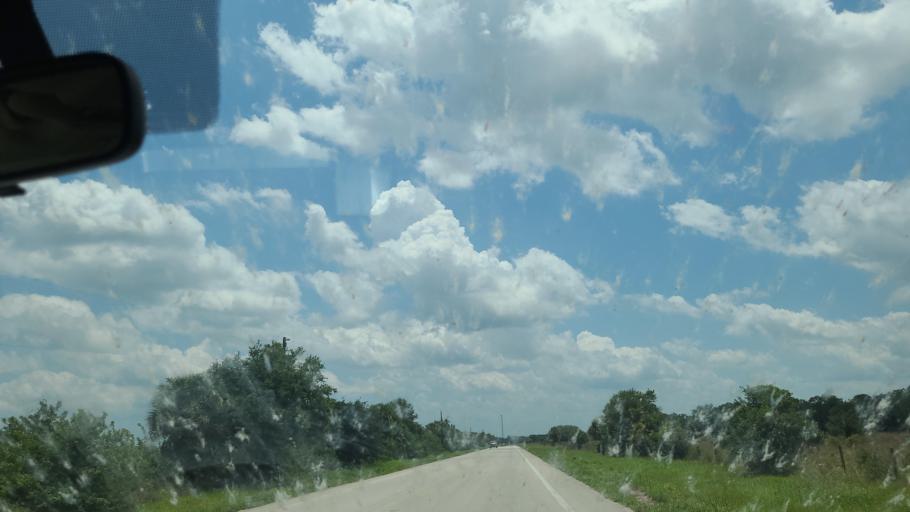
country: US
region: Florida
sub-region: Glades County
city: Buckhead Ridge
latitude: 27.1388
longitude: -81.0916
